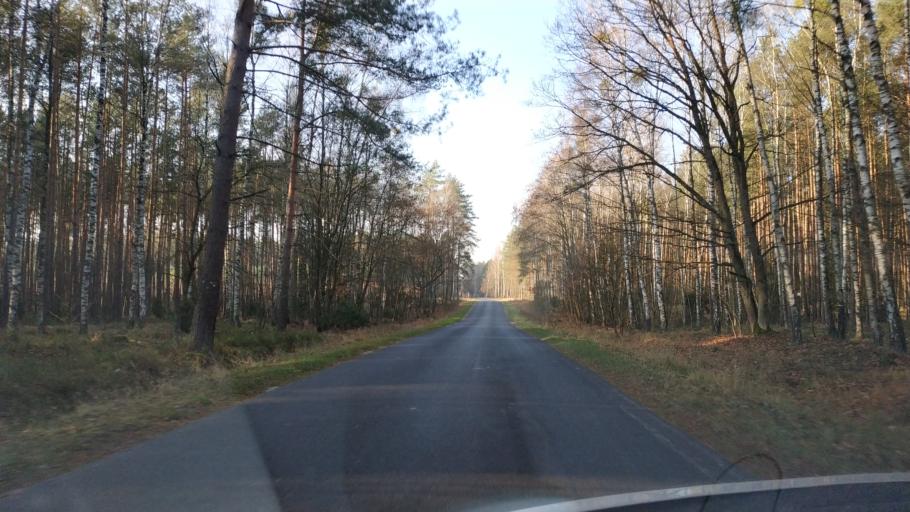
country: PL
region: Warmian-Masurian Voivodeship
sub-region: Powiat nowomiejski
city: Biskupiec
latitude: 53.4492
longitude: 19.4195
